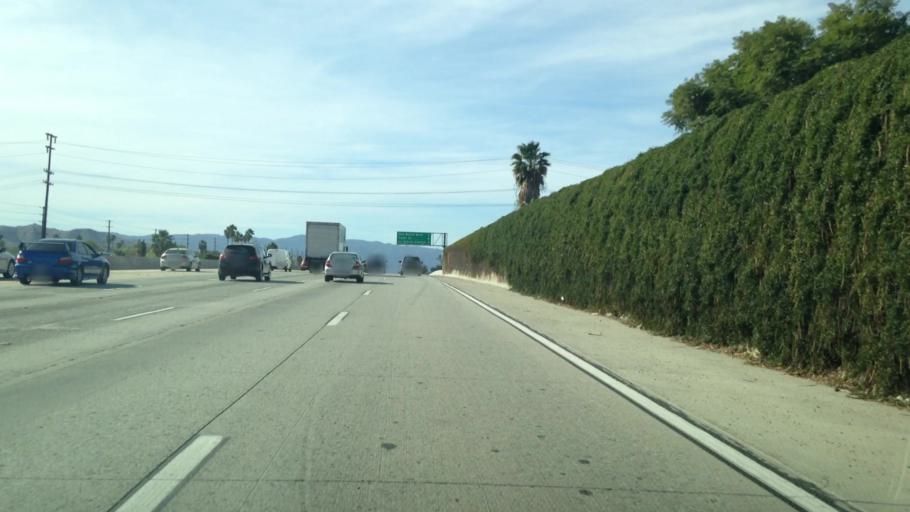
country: US
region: California
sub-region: Riverside County
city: Riverside
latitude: 33.9242
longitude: -117.4258
